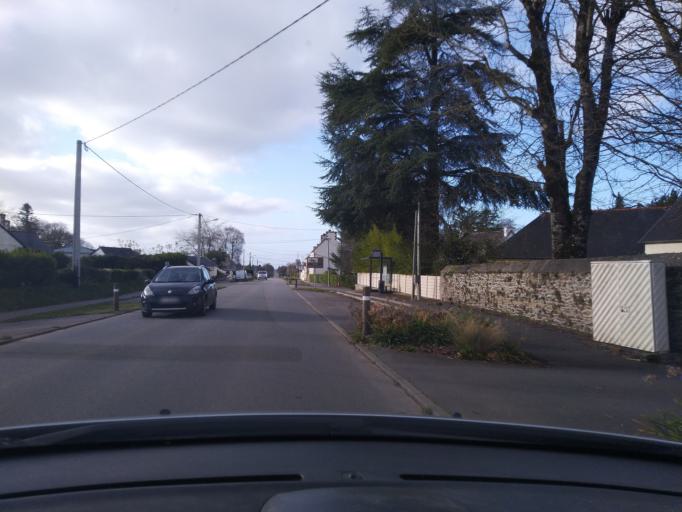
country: FR
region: Brittany
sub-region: Departement du Finistere
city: Plourin-les-Morlaix
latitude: 48.5755
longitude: -3.7641
